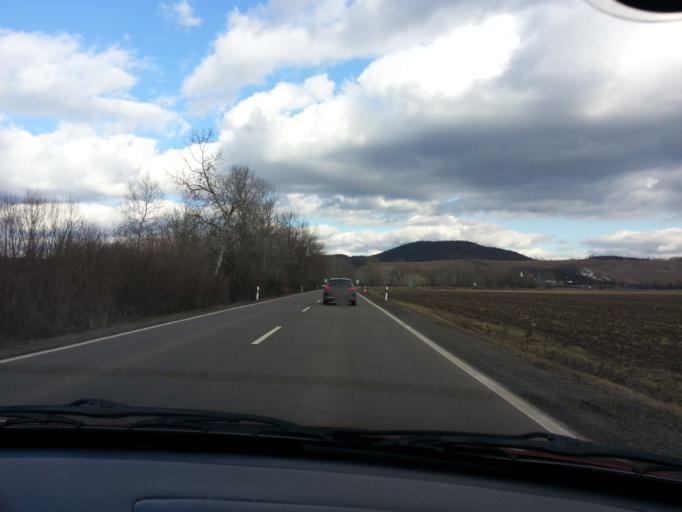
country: HU
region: Nograd
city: Tar
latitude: 47.9592
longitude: 19.7332
